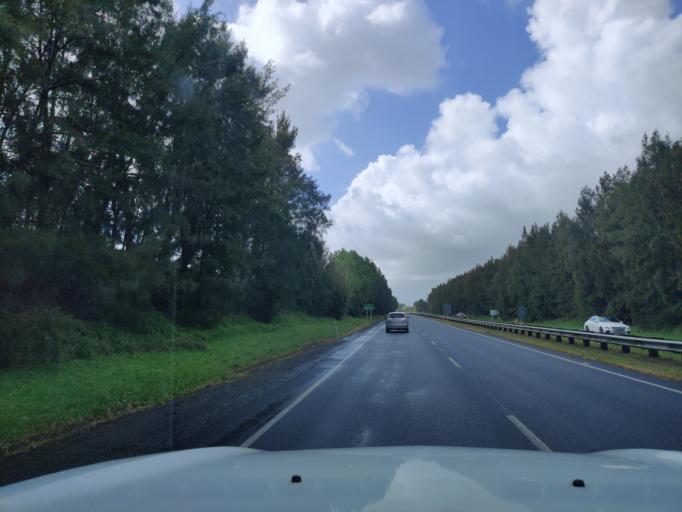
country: NZ
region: Waikato
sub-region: Hamilton City
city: Hamilton
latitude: -37.8319
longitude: 175.3611
